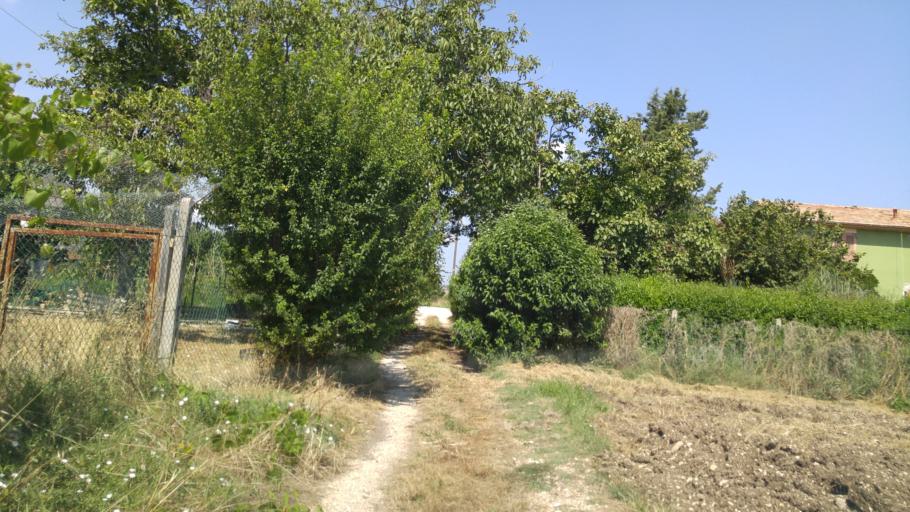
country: IT
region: The Marches
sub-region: Provincia di Pesaro e Urbino
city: Cuccurano
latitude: 43.7707
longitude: 12.9661
